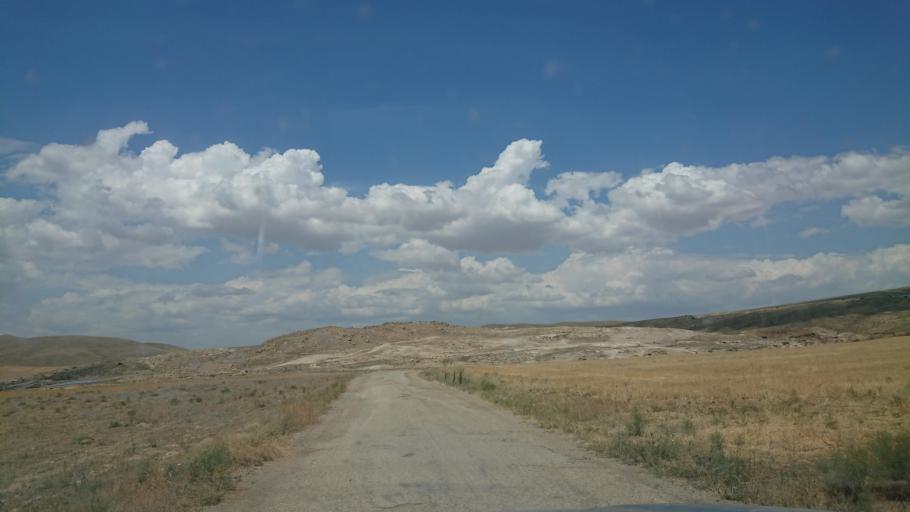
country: TR
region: Aksaray
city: Sariyahsi
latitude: 38.9946
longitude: 33.9139
